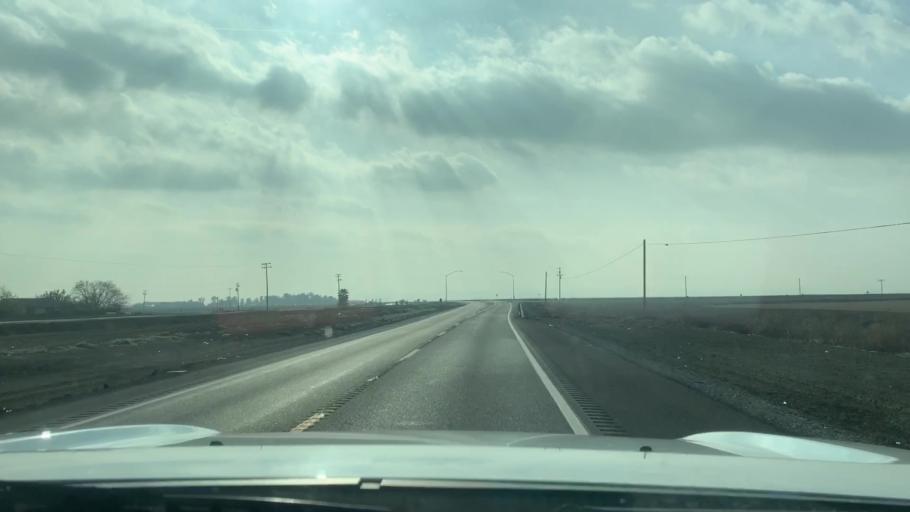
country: US
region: California
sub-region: Kings County
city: Stratford
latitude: 36.1394
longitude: -119.8770
